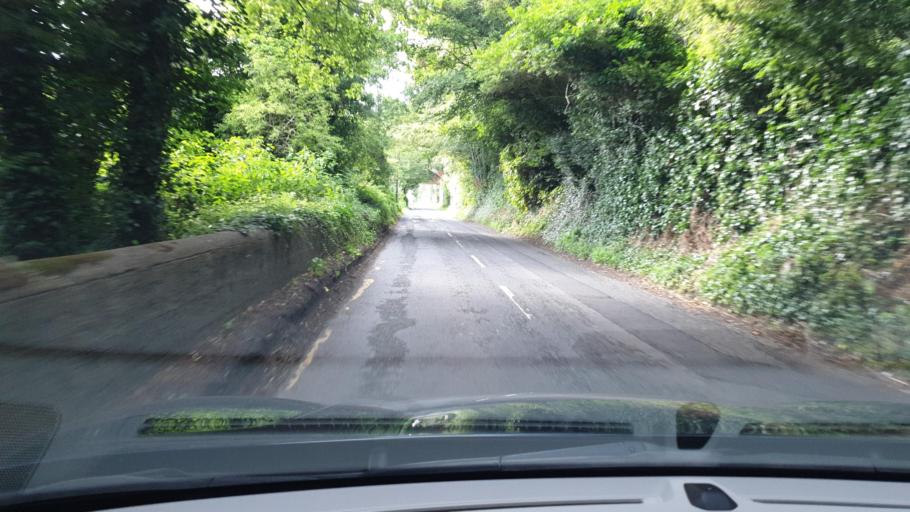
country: IE
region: Leinster
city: Castleknock
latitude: 53.3607
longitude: -6.3634
